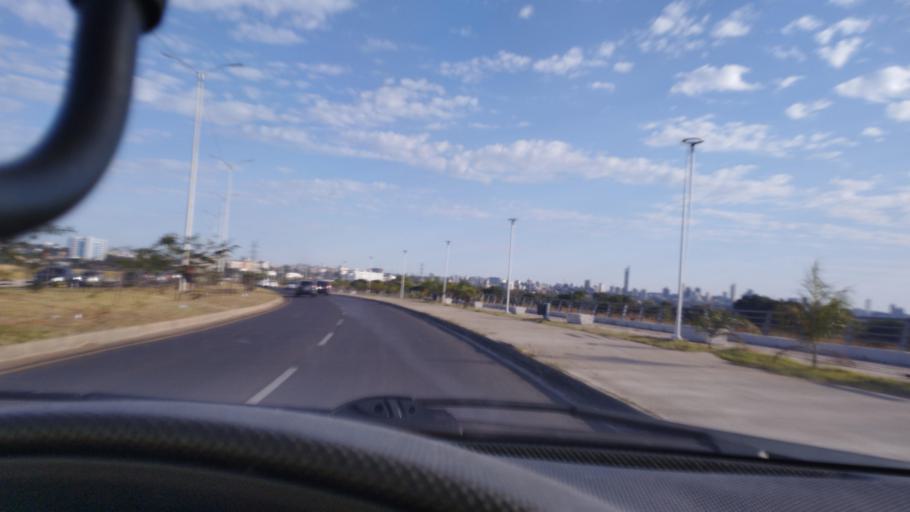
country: PY
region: Asuncion
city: Asuncion
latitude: -25.2568
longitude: -57.6080
